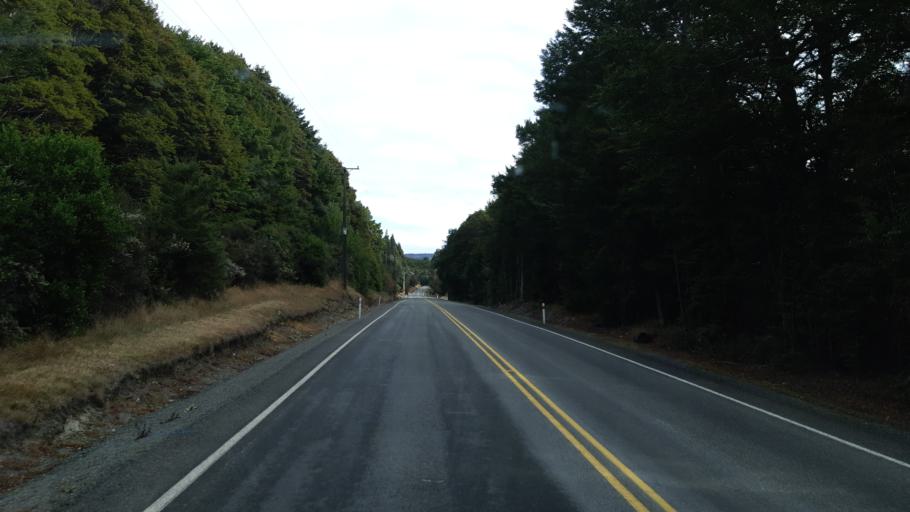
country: NZ
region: Tasman
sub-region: Tasman District
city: Wakefield
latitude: -41.7766
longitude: 172.9235
